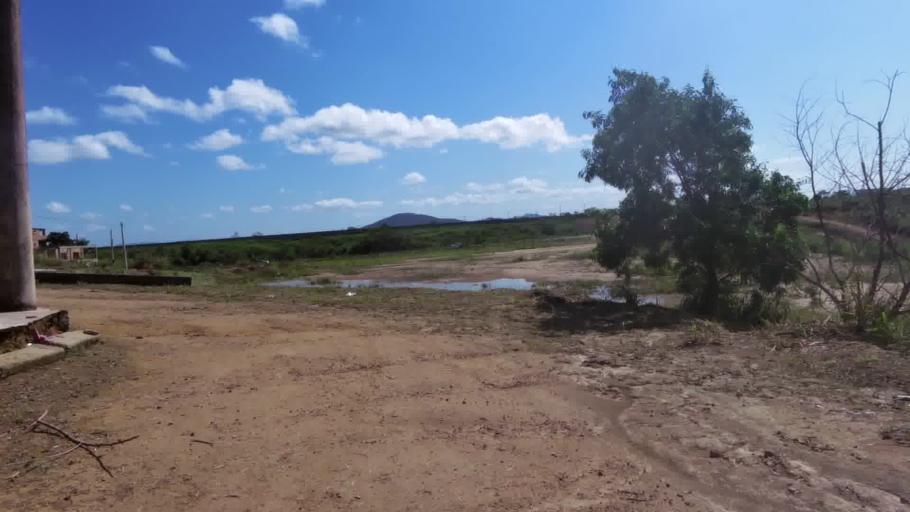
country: BR
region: Espirito Santo
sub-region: Piuma
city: Piuma
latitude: -20.8014
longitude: -40.5978
